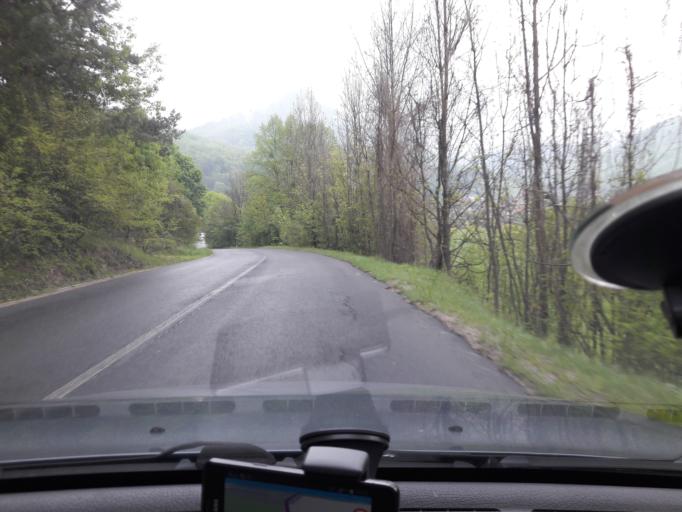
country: SK
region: Banskobystricky
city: Revuca
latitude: 48.7361
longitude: 20.0375
